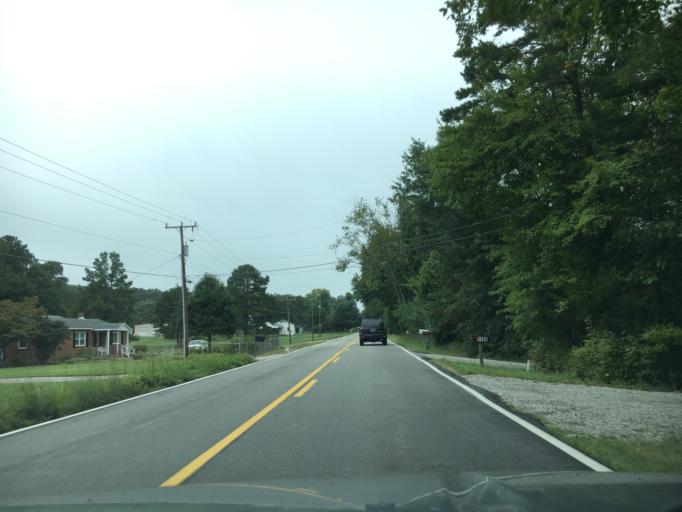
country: US
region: Virginia
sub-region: Powhatan County
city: Powhatan
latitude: 37.4824
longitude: -77.8026
